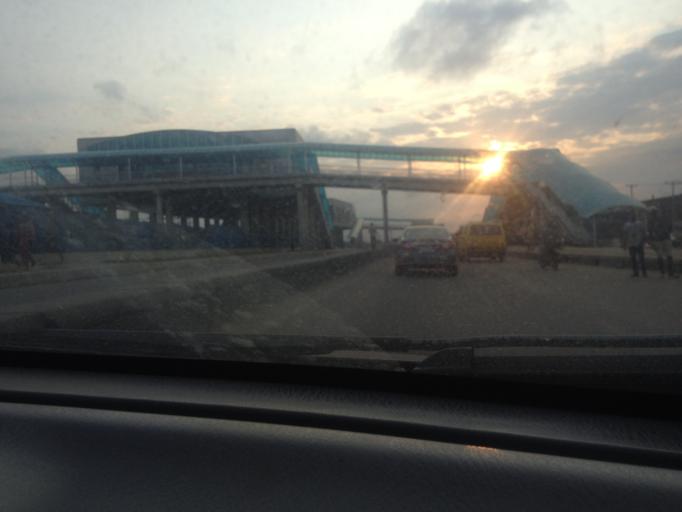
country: NG
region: Lagos
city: Ajegunle
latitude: 6.4602
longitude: 3.3132
